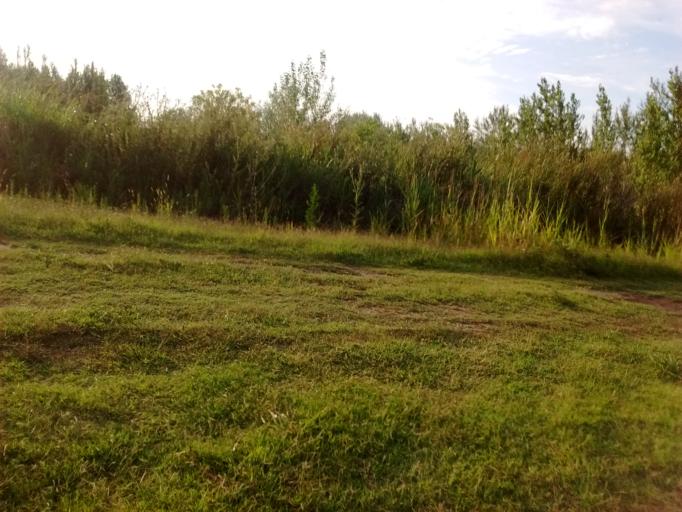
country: AR
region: Santa Fe
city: Roldan
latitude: -32.9263
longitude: -60.8768
